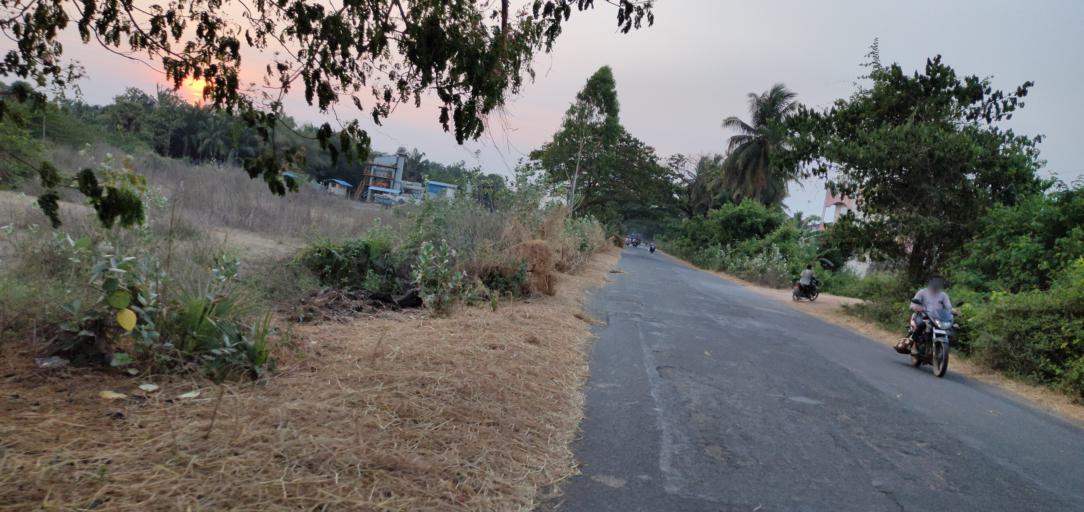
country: IN
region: Andhra Pradesh
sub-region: West Godavari
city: Tadepallegudem
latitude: 16.8506
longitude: 81.4872
